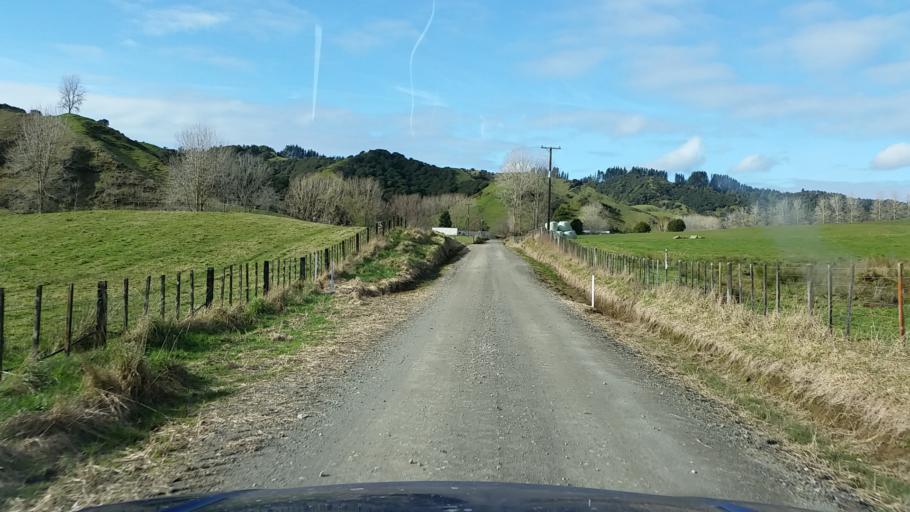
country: NZ
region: Taranaki
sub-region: South Taranaki District
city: Eltham
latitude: -39.2598
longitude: 174.5869
